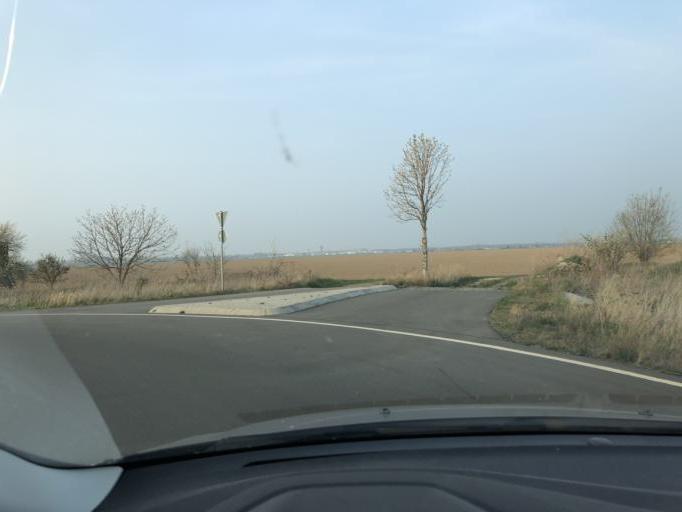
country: DE
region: Saxony
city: Dobernitz
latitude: 51.4962
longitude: 12.3223
